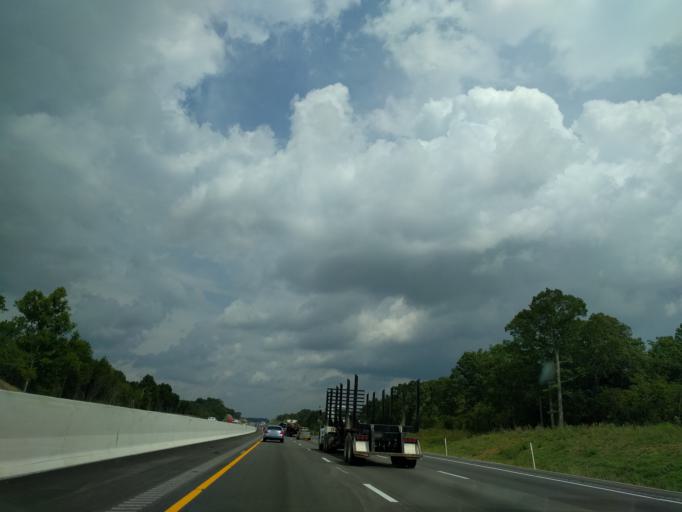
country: US
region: Kentucky
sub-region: Hart County
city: Munfordville
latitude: 37.4106
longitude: -85.8815
